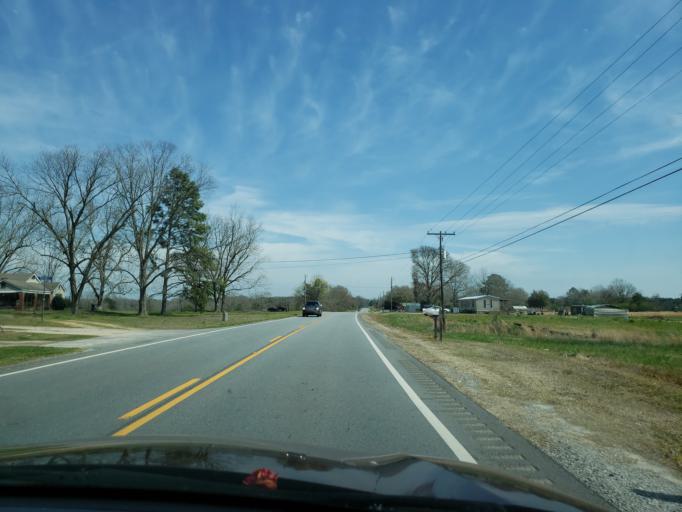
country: US
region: Alabama
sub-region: Elmore County
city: Tallassee
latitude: 32.5598
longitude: -85.8066
